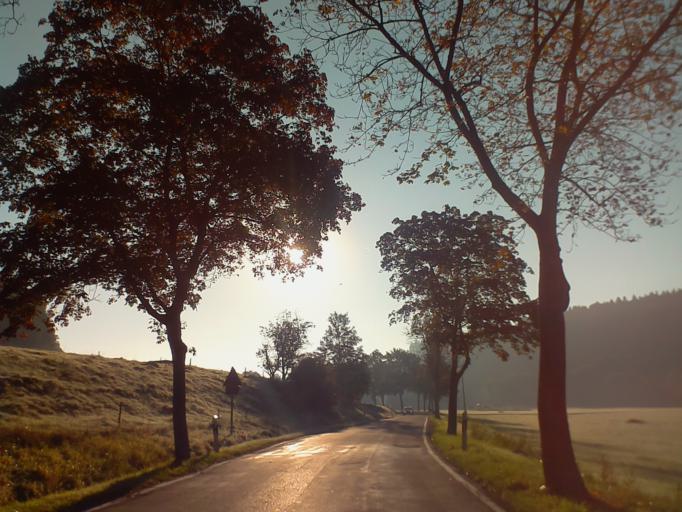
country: DE
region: Thuringia
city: Rattelsdorf
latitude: 50.8317
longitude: 11.7701
